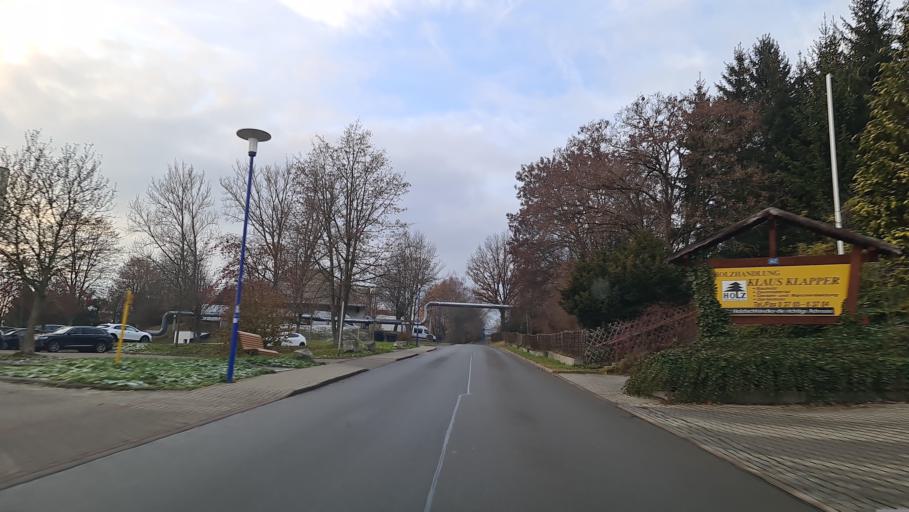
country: DE
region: Saxony
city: Mylau
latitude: 50.6238
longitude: 12.2811
